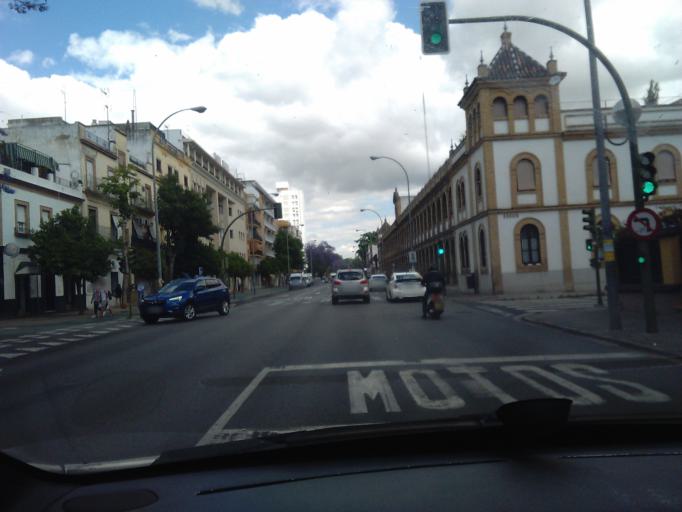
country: ES
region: Andalusia
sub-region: Provincia de Sevilla
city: Sevilla
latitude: 37.3757
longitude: -5.9706
